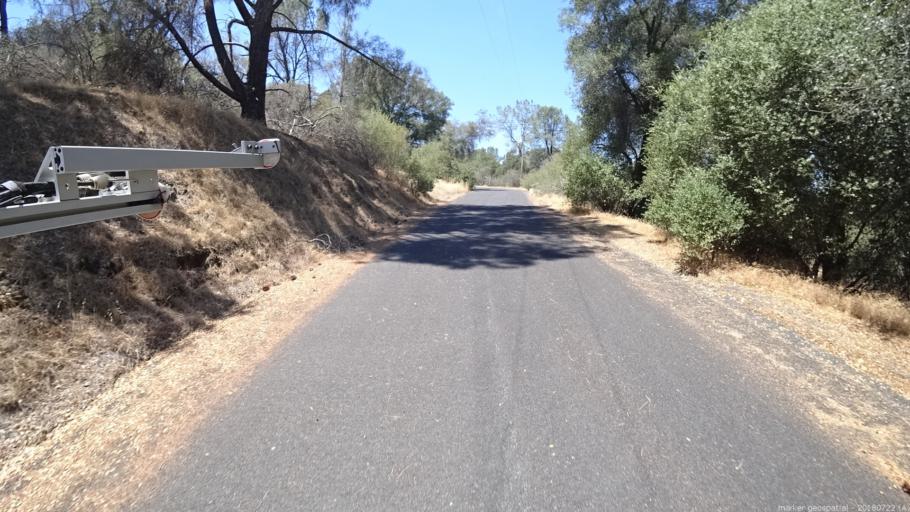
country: US
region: California
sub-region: Madera County
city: Yosemite Lakes
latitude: 37.2128
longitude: -119.7310
